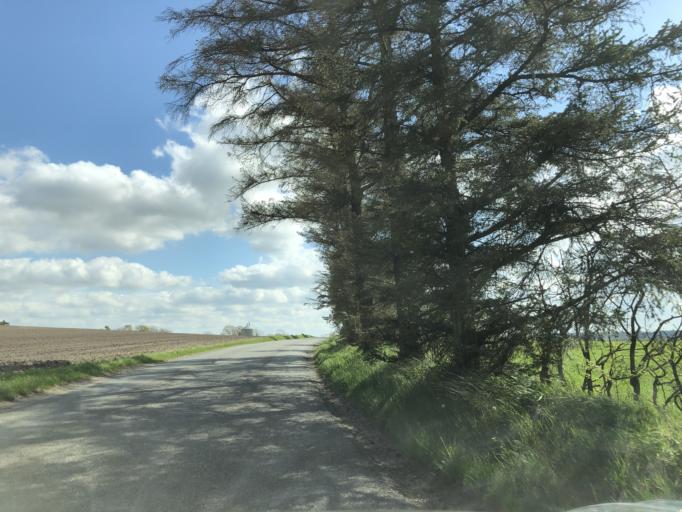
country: DK
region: Central Jutland
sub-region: Herning Kommune
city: Avlum
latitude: 56.2814
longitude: 8.6977
